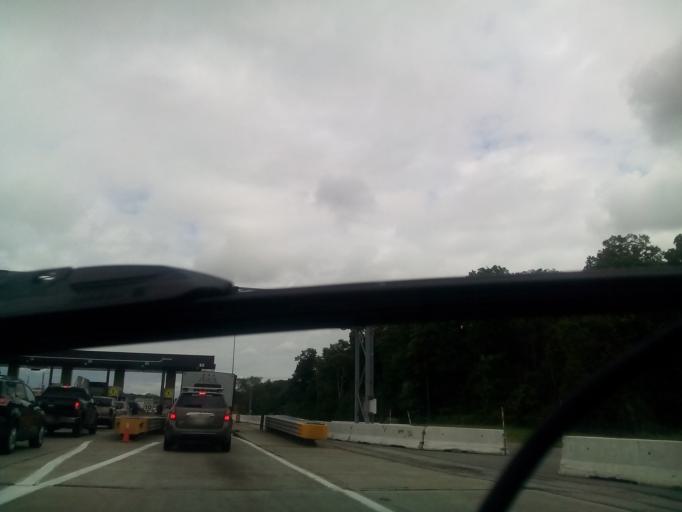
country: US
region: Ohio
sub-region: Williams County
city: Montpelier
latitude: 41.6290
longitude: -84.7552
